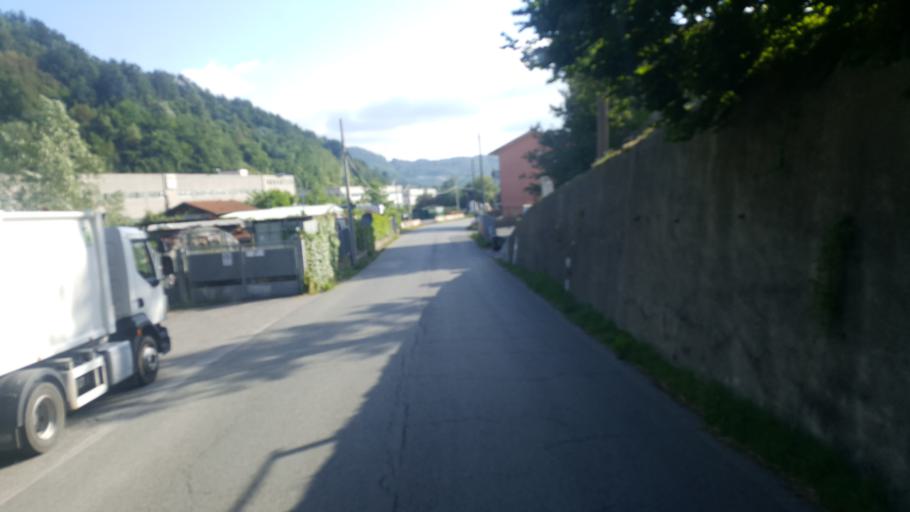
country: IT
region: Liguria
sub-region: Provincia di Genova
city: Savignone
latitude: 44.5788
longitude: 8.9688
